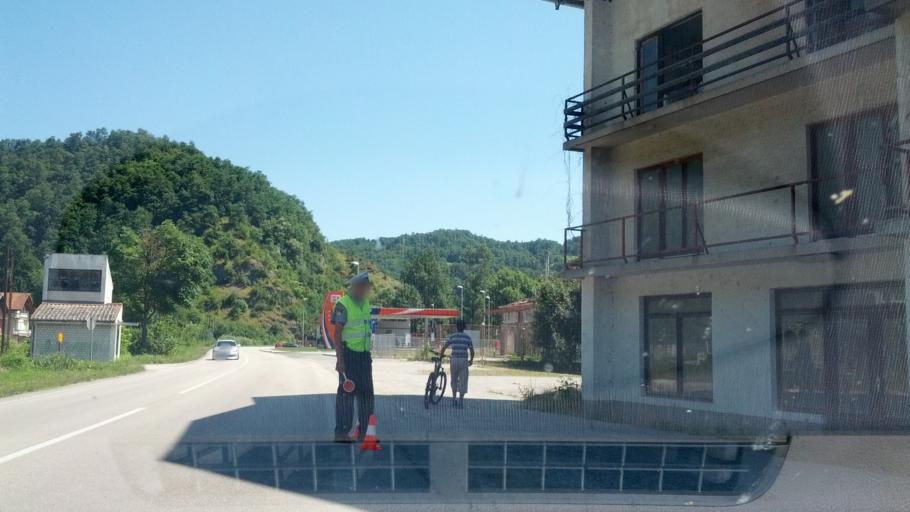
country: BA
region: Federation of Bosnia and Herzegovina
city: Bosanska Krupa
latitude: 44.8985
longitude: 16.1583
